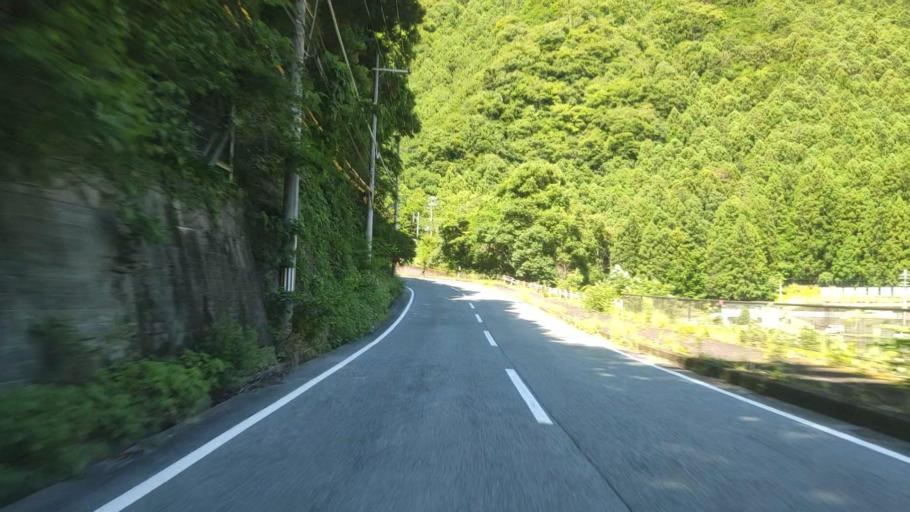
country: JP
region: Nara
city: Yoshino-cho
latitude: 34.2951
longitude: 136.0025
